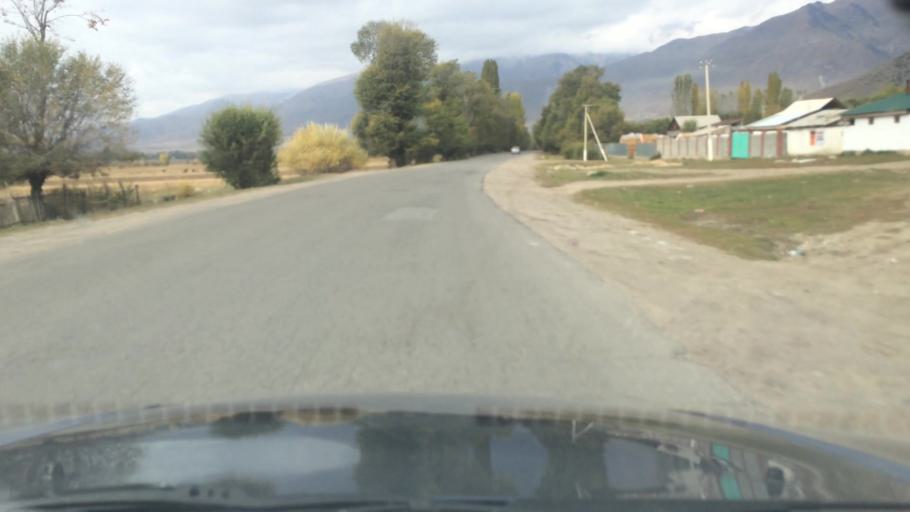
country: KG
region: Ysyk-Koel
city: Tyup
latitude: 42.7824
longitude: 78.2827
